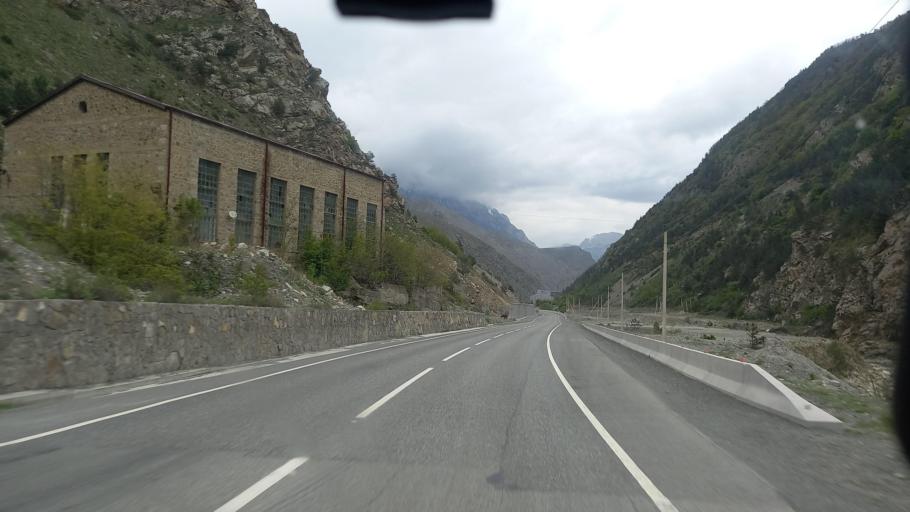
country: RU
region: North Ossetia
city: Mizur
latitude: 42.8392
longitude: 44.0285
